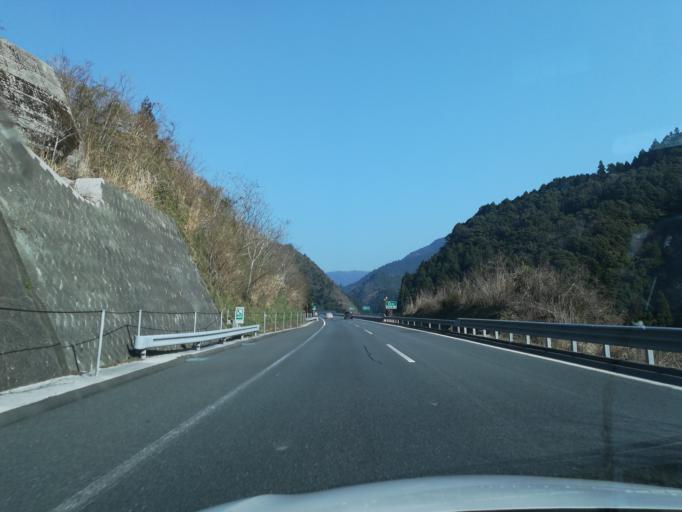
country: JP
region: Ehime
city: Kawanoecho
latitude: 33.8224
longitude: 133.6629
